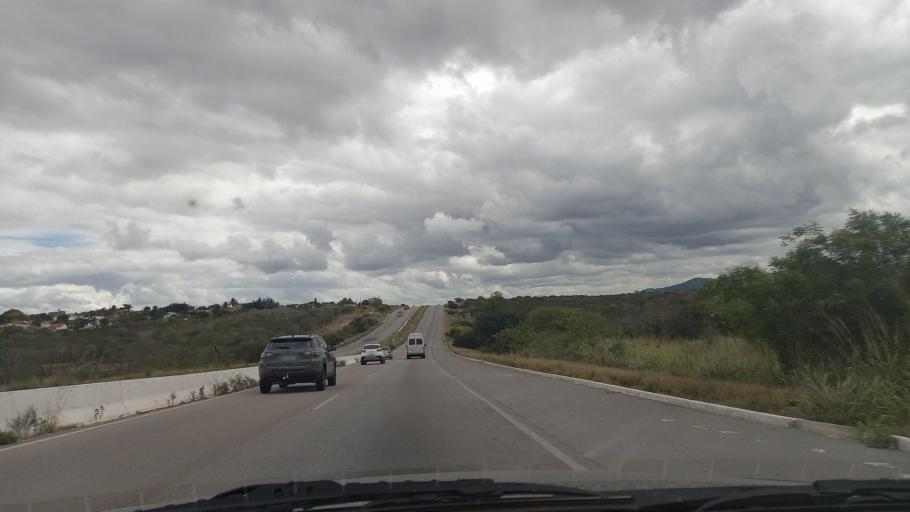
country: BR
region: Pernambuco
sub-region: Caruaru
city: Caruaru
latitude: -8.3187
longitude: -36.0610
